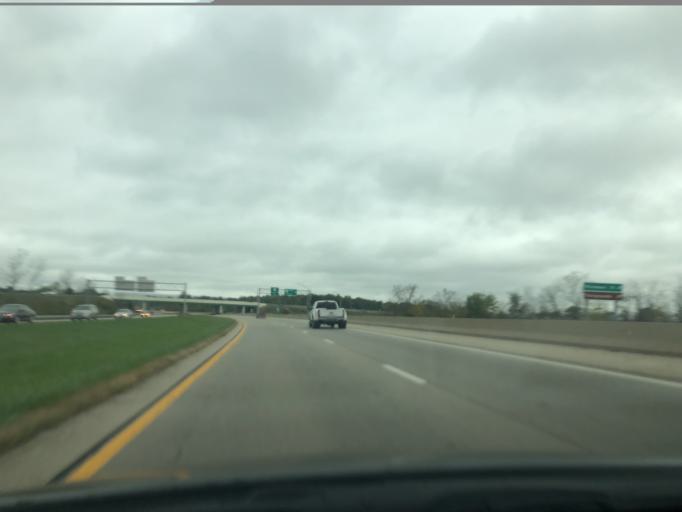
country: US
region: Ohio
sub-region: Union County
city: Marysville
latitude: 40.2516
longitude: -83.3636
